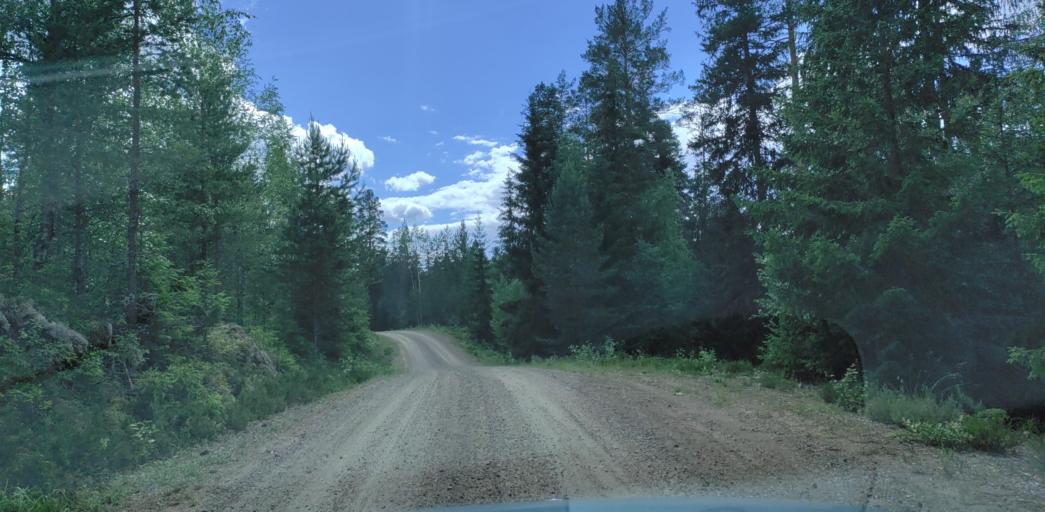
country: SE
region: Vaermland
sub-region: Hagfors Kommun
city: Ekshaerad
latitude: 60.0785
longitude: 13.2918
